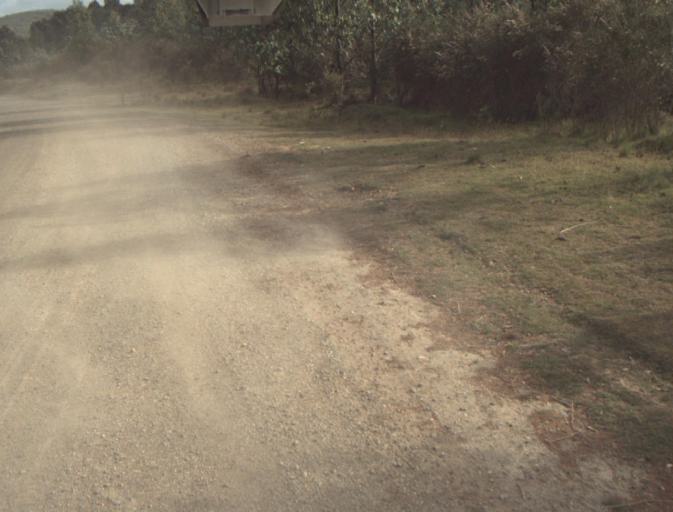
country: AU
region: Tasmania
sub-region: Dorset
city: Scottsdale
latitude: -41.3733
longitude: 147.4740
